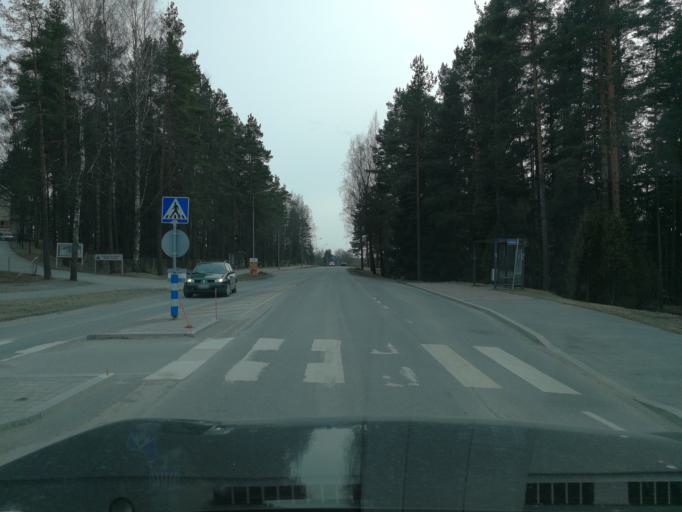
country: FI
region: Uusimaa
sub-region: Helsinki
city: Lohja
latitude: 60.1857
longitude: 23.9952
